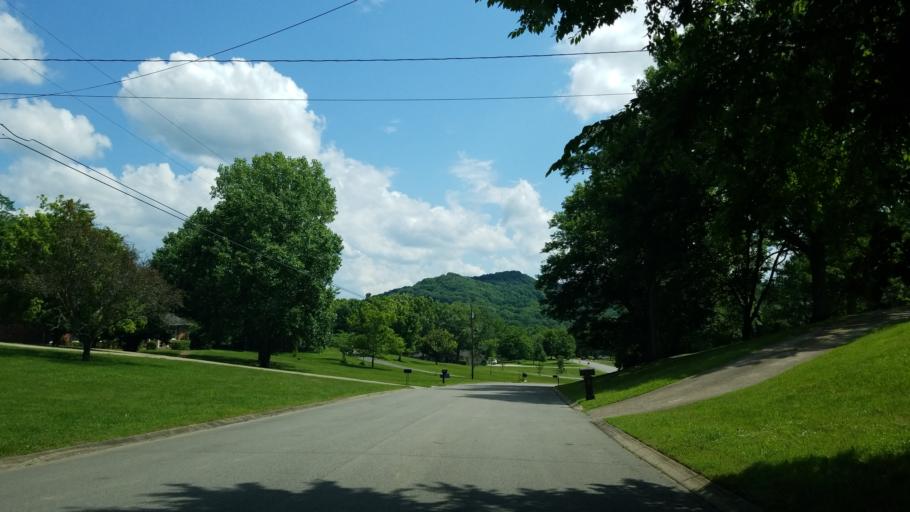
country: US
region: Tennessee
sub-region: Davidson County
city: Forest Hills
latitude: 36.0319
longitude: -86.8505
